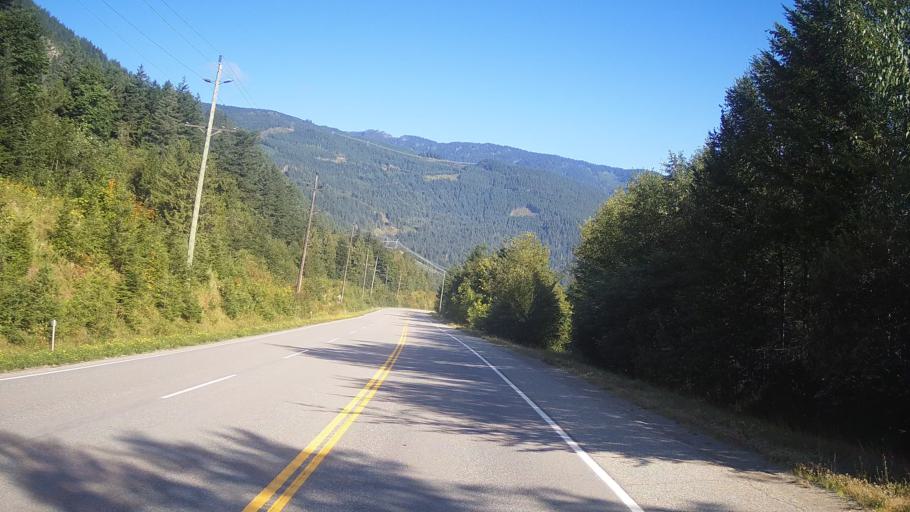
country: CA
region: British Columbia
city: Hope
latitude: 49.5328
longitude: -121.4259
